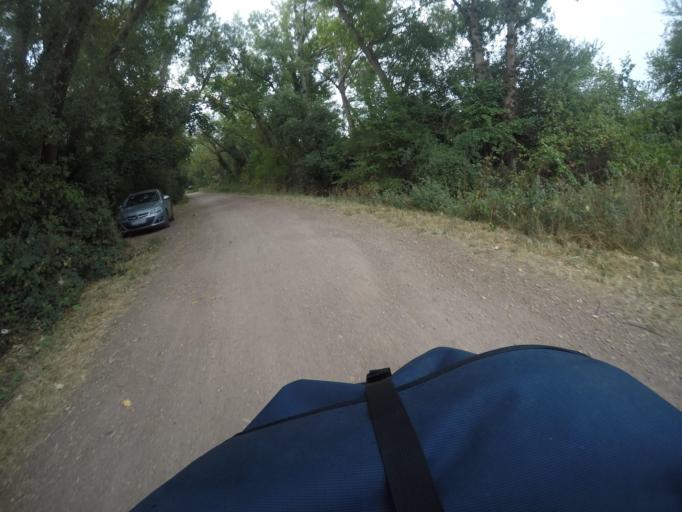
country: DE
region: Hesse
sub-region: Regierungsbezirk Darmstadt
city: Rudesheim am Rhein
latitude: 49.9706
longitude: 7.9416
